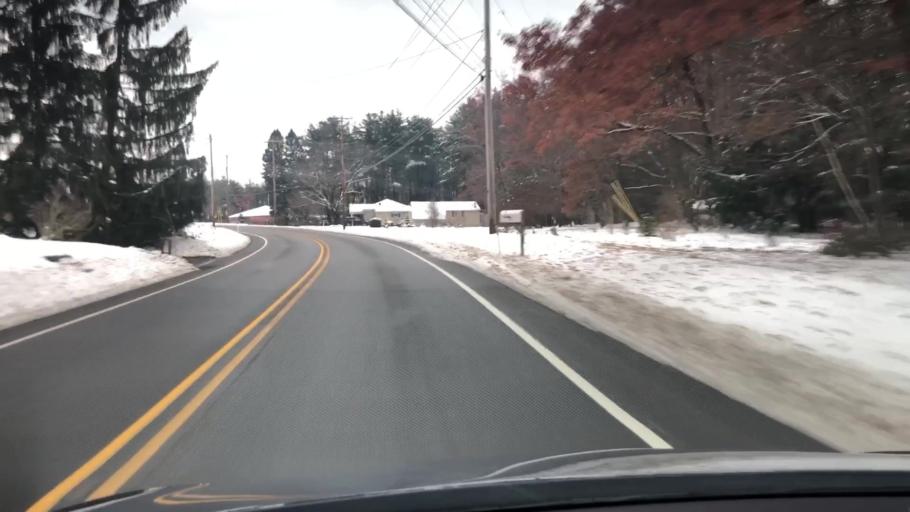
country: US
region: Pennsylvania
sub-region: Jefferson County
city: Brookville
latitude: 41.1605
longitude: -79.0541
